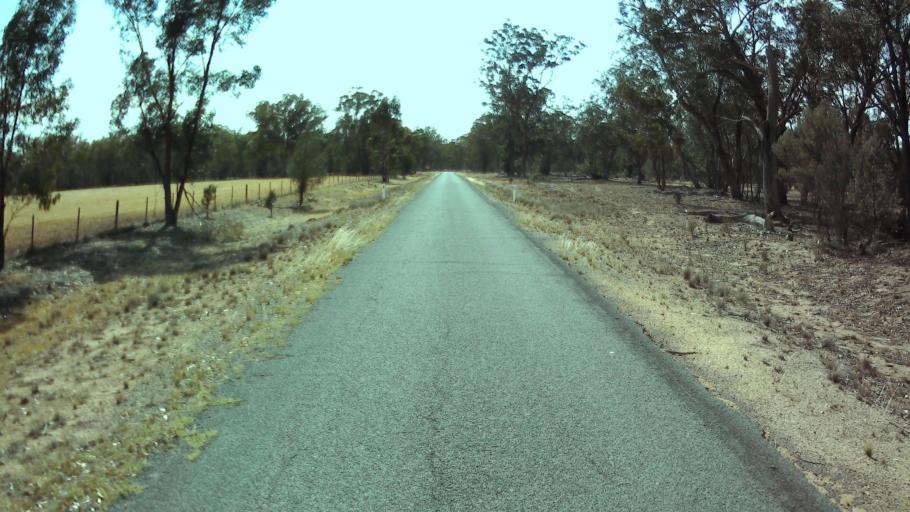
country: AU
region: New South Wales
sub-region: Weddin
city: Grenfell
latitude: -33.7568
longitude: 148.0789
